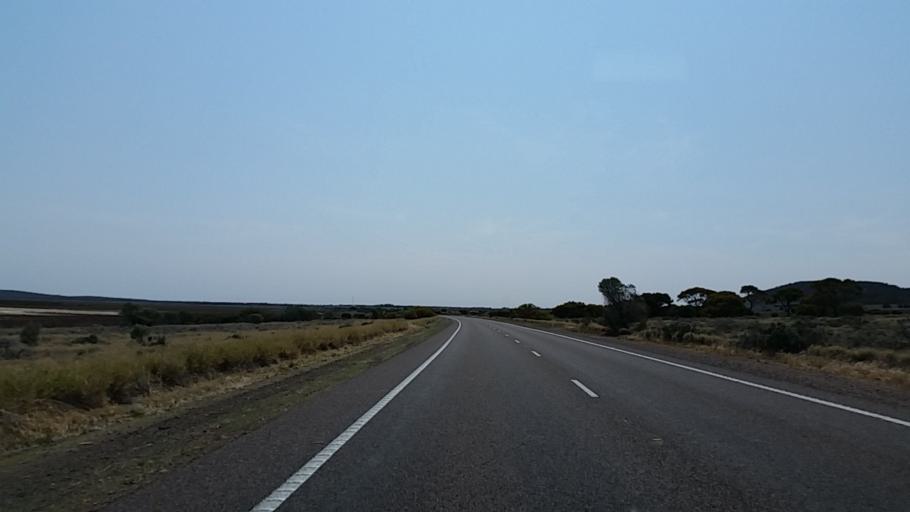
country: AU
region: South Australia
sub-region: Port Augusta
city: Port Augusta
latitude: -32.7652
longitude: 137.9531
